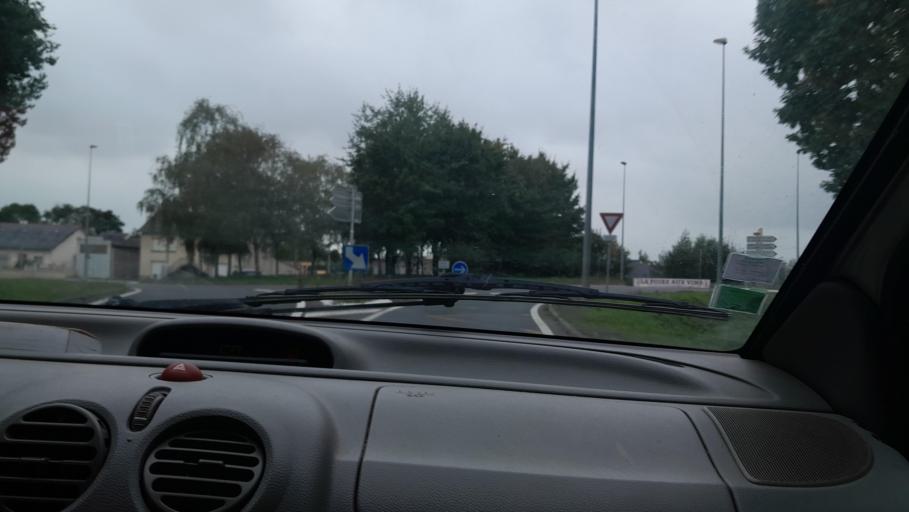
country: FR
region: Pays de la Loire
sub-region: Departement de la Loire-Atlantique
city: Saint-Mars-la-Jaille
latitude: 47.5298
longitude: -1.1846
